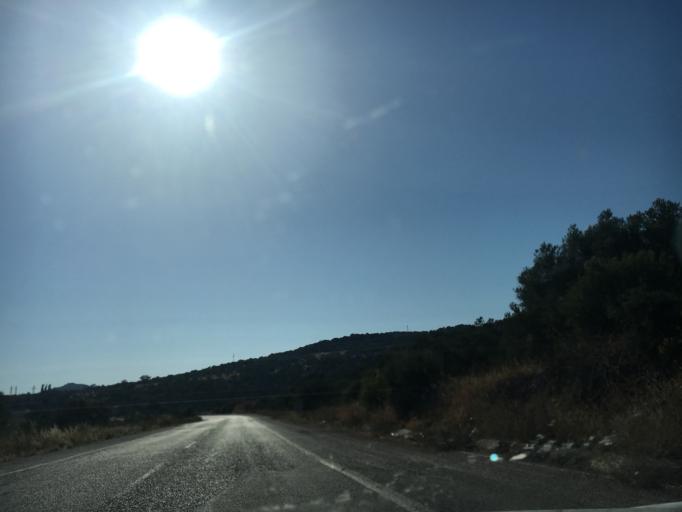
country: TR
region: Canakkale
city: Behram
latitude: 39.5066
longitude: 26.4089
